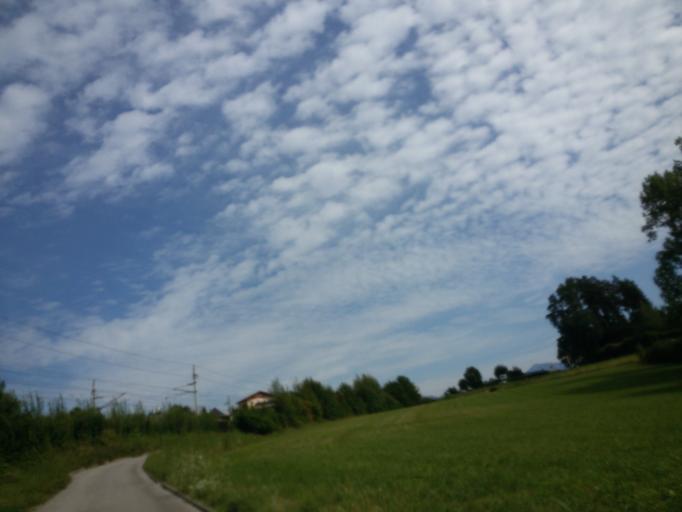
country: AT
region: Carinthia
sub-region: Politischer Bezirk Klagenfurt Land
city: Maria Worth
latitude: 46.6334
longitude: 14.1596
